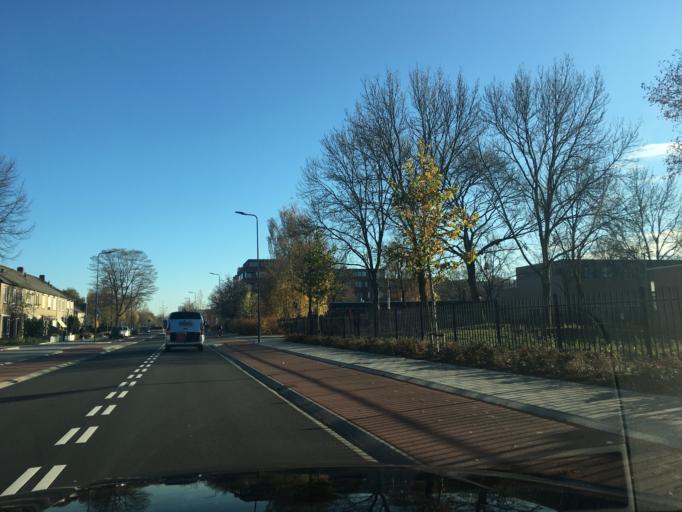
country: NL
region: North Brabant
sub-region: Gemeente 's-Hertogenbosch
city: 's-Hertogenbosch
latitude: 51.6988
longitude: 5.2641
